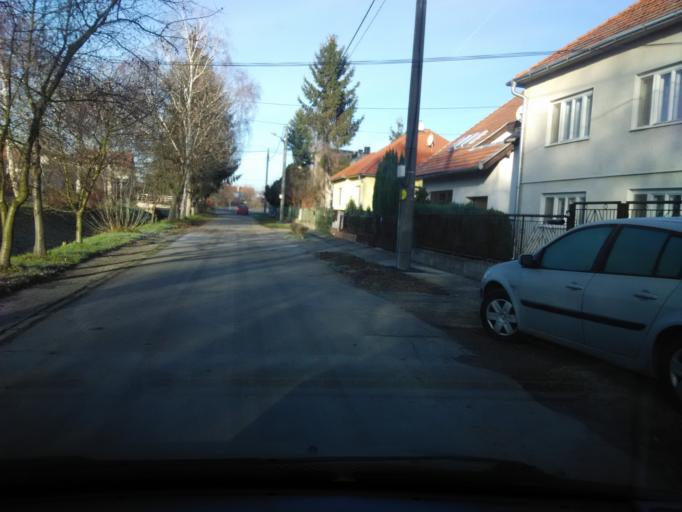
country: SK
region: Nitriansky
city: Tlmace
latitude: 48.3170
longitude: 18.5280
